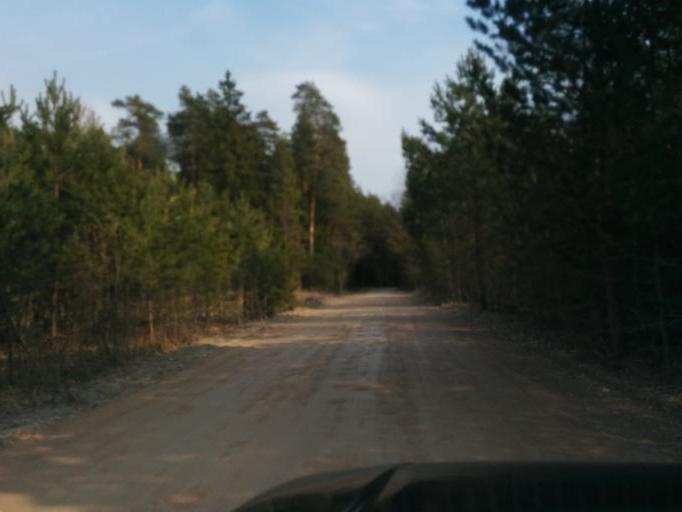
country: LV
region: Olaine
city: Olaine
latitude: 56.7889
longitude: 24.0457
